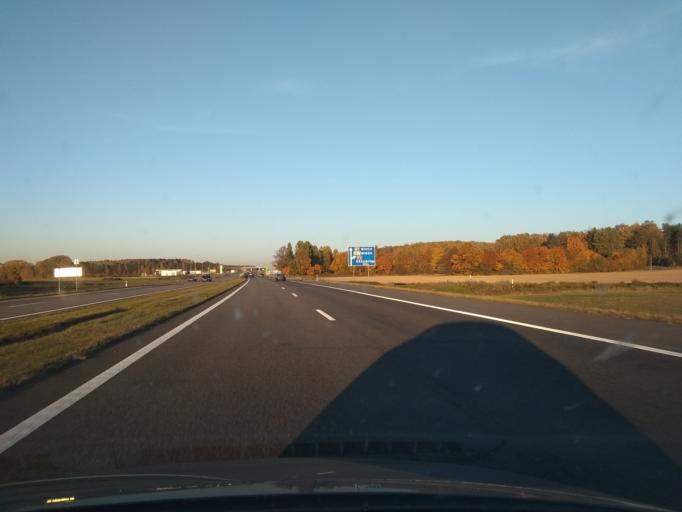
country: BY
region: Brest
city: Baranovichi
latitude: 53.1879
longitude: 26.0695
